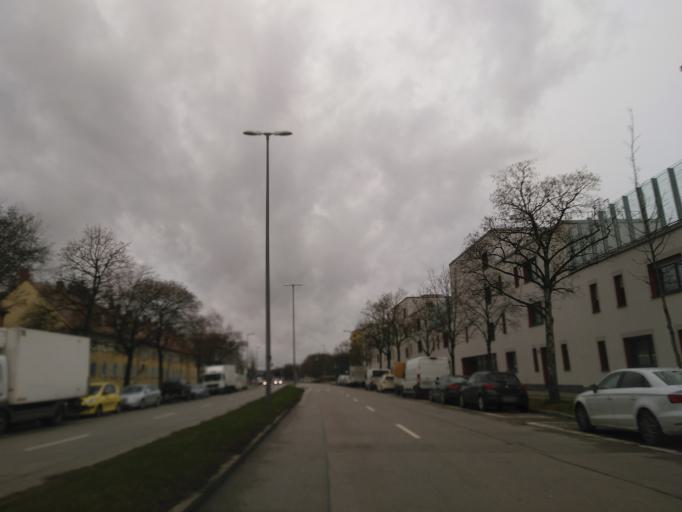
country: DE
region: Bavaria
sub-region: Upper Bavaria
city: Bogenhausen
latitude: 48.1199
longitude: 11.6260
